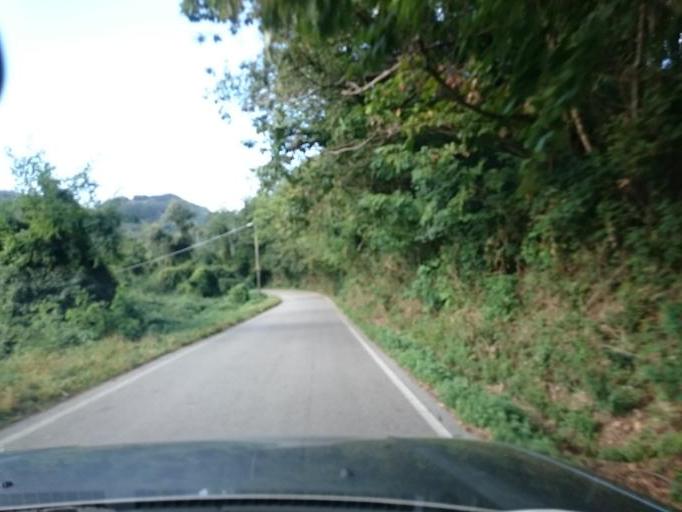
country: IT
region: Veneto
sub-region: Provincia di Padova
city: Galzignano
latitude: 45.3219
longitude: 11.7070
